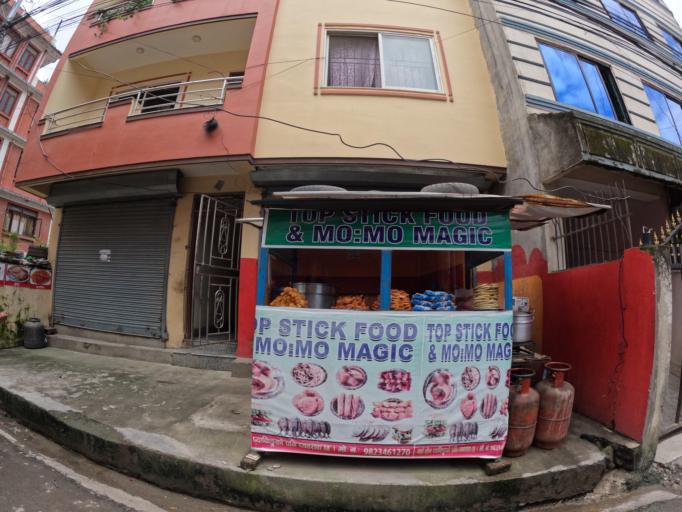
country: NP
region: Central Region
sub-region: Bagmati Zone
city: Kathmandu
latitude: 27.7386
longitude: 85.3122
